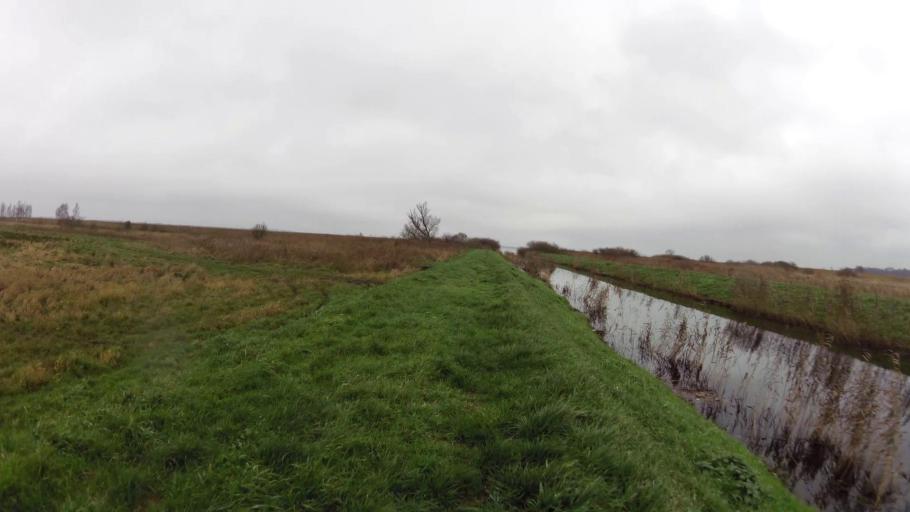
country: PL
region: West Pomeranian Voivodeship
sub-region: Koszalin
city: Koszalin
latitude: 54.2497
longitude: 16.1319
